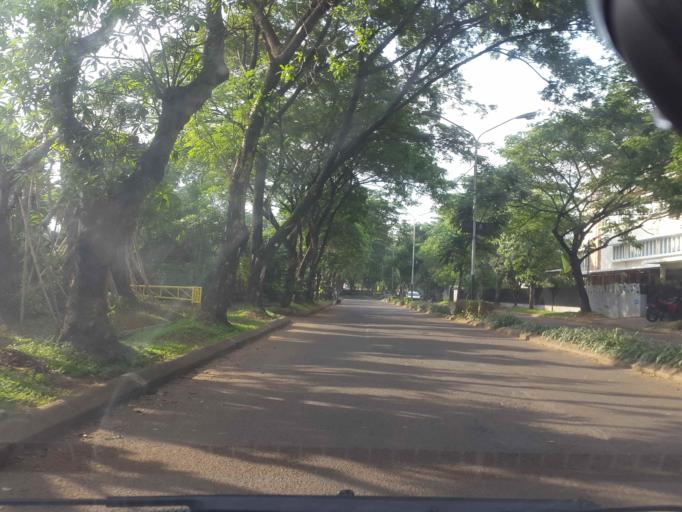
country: ID
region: Banten
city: South Tangerang
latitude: -6.2754
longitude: 106.6945
